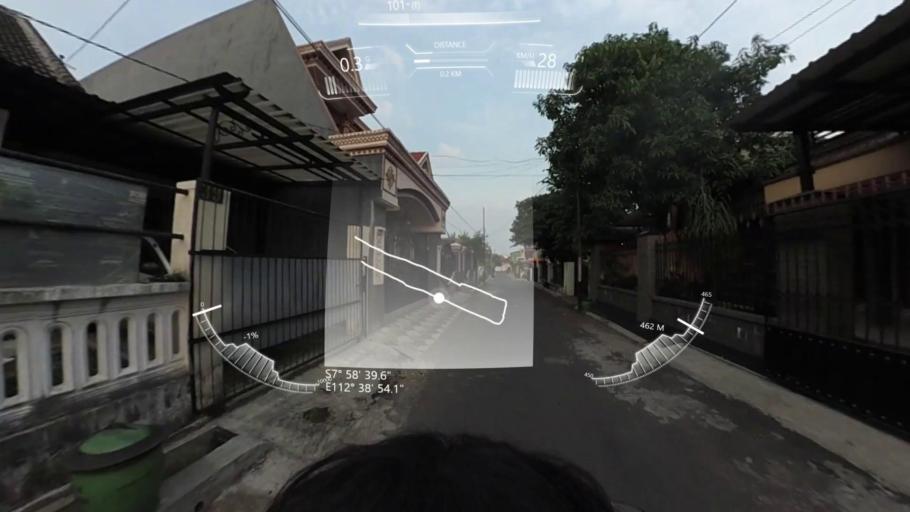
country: ID
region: East Java
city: Malang
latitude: -7.9777
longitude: 112.6484
